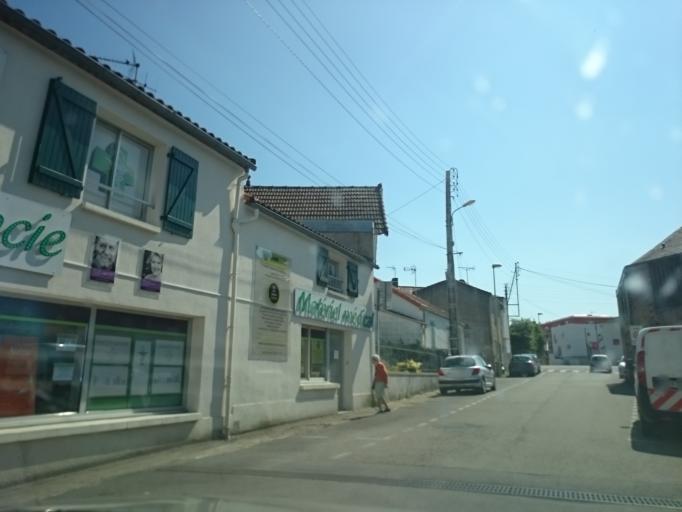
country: FR
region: Pays de la Loire
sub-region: Departement de la Loire-Atlantique
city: Le Pellerin
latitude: 47.1997
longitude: -1.7522
